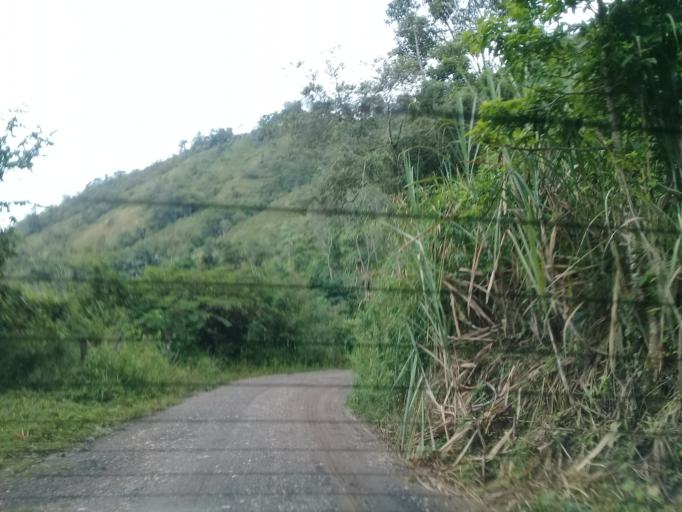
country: CO
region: Cundinamarca
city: Quipile
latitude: 4.6670
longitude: -74.5520
